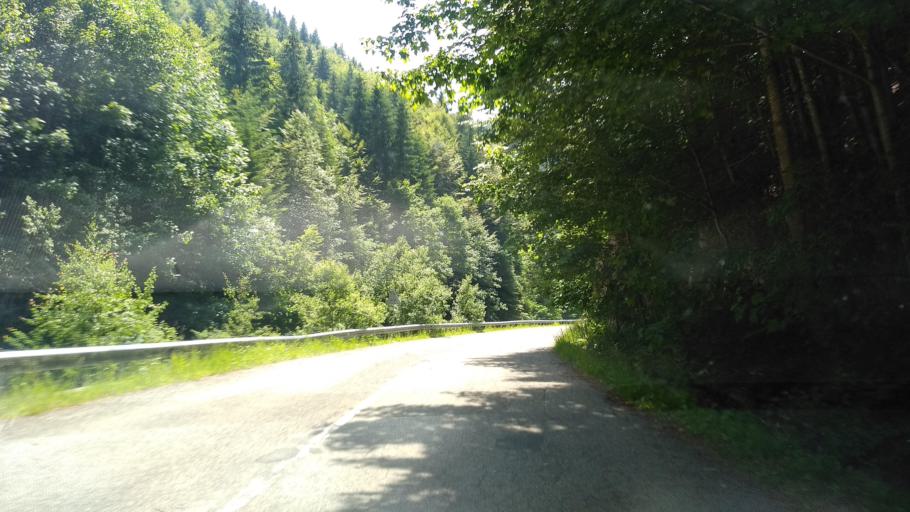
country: RO
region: Hunedoara
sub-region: Comuna Uricani
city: Uricani
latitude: 45.2768
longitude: 22.9612
